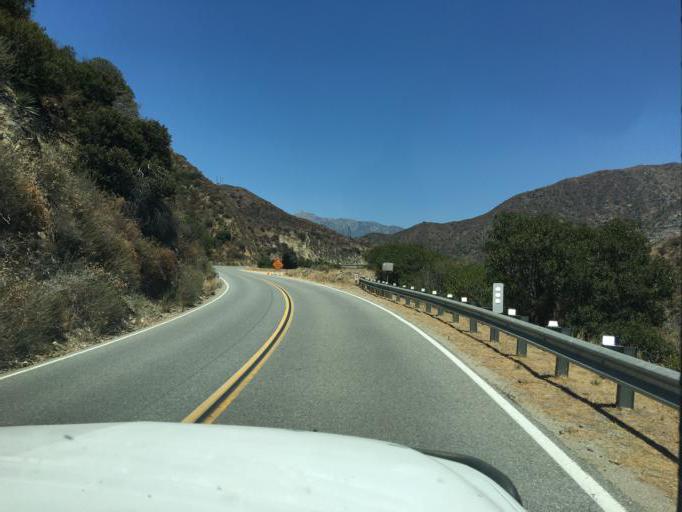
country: US
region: California
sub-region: Los Angeles County
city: Glendora
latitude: 34.1941
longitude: -117.8639
